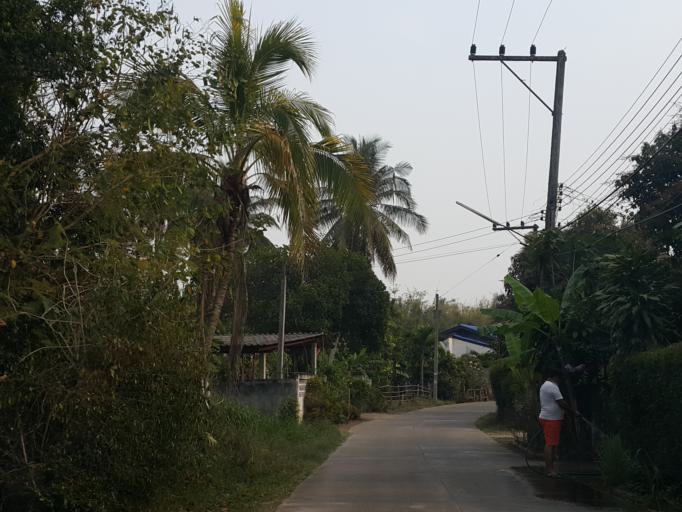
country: TH
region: Chiang Mai
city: San Sai
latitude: 18.9530
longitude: 98.9190
